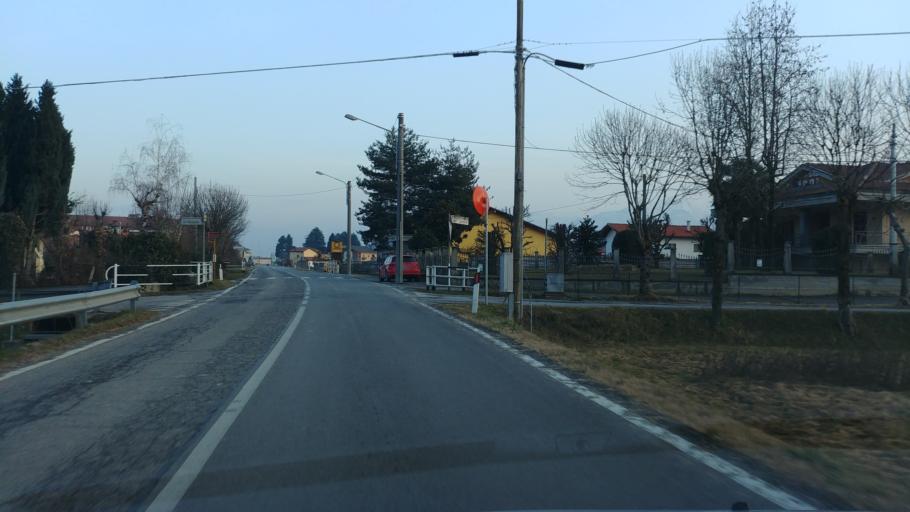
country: IT
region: Piedmont
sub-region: Provincia di Cuneo
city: Cuneo
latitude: 44.4029
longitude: 7.5267
